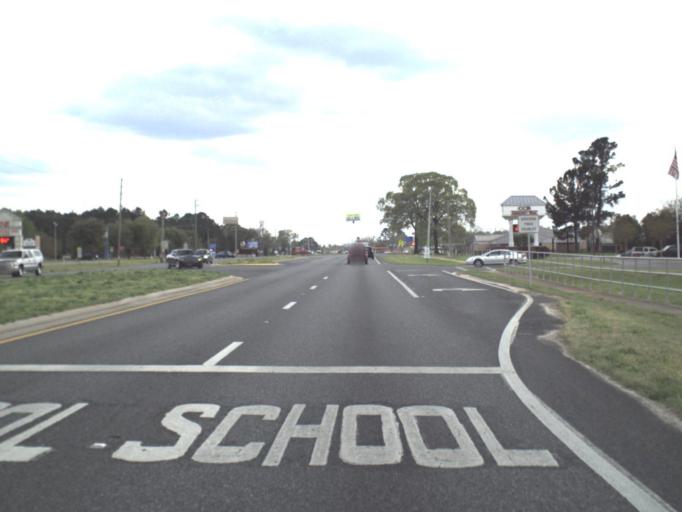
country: US
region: Florida
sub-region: Okaloosa County
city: Crestview
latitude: 30.7925
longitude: -86.5580
